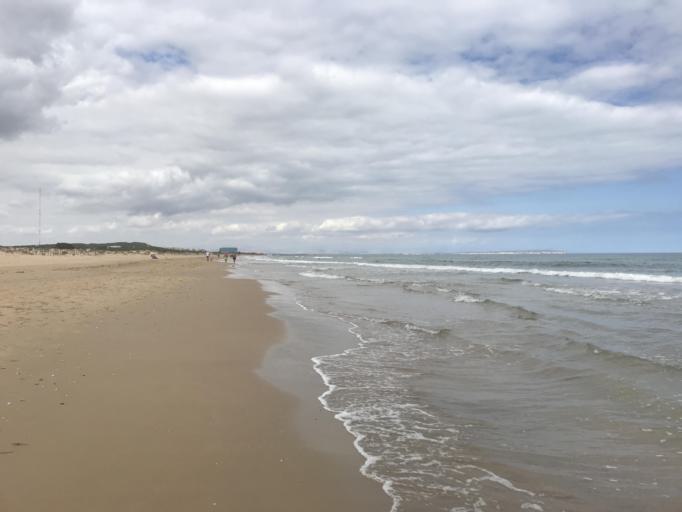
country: ES
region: Valencia
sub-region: Provincia de Alicante
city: Guardamar del Segura
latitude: 38.0371
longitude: -0.6516
